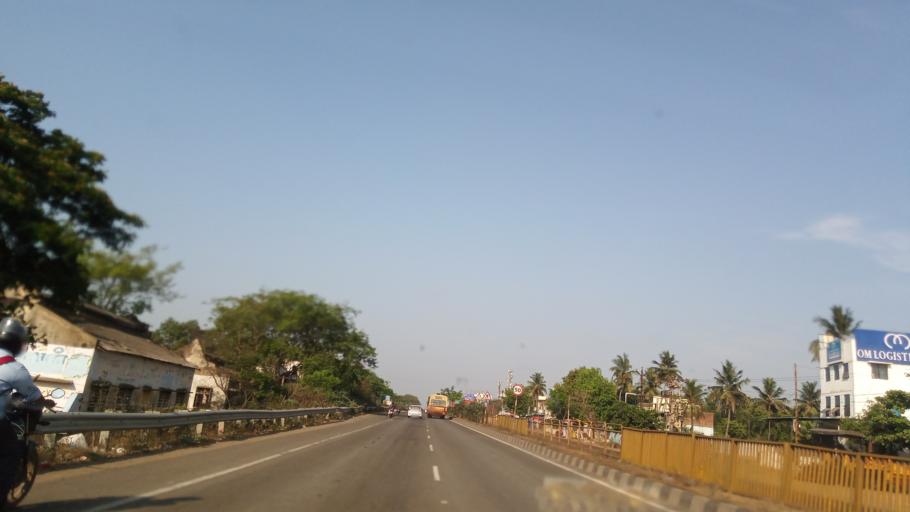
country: IN
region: Tamil Nadu
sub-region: Kancheepuram
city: Poonamalle
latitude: 13.0394
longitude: 80.0543
